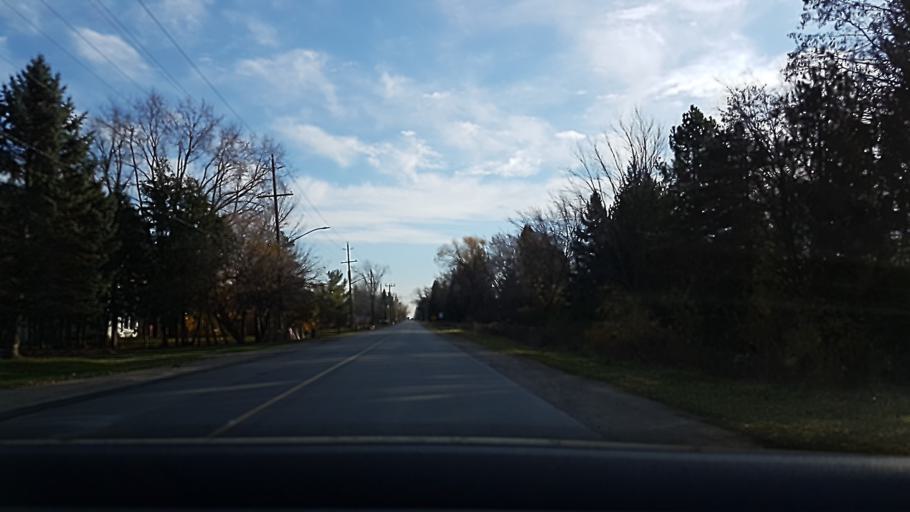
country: CA
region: Ontario
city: Innisfil
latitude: 44.3569
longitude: -79.5500
